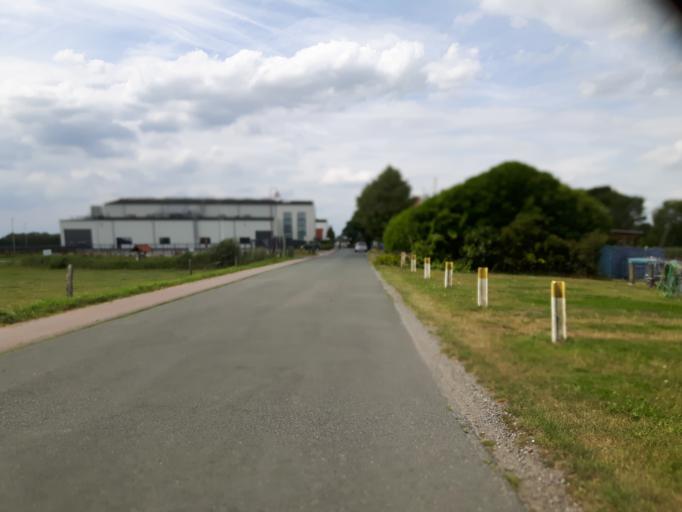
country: DE
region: Lower Saxony
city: Varel
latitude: 53.4078
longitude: 8.1759
